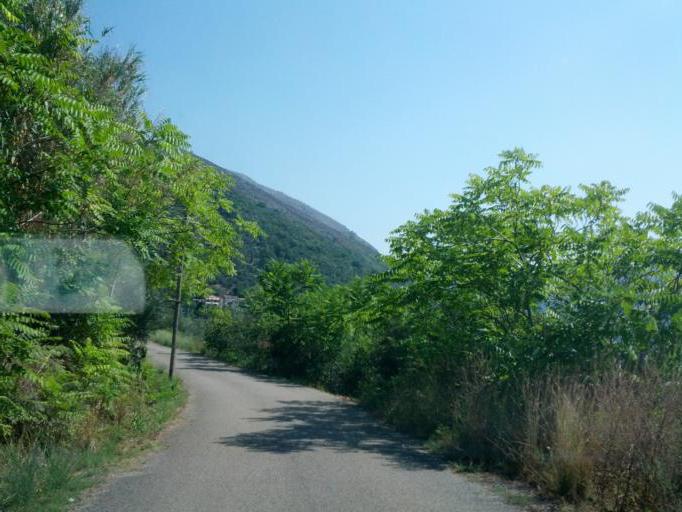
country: IT
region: Latium
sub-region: Provincia di Latina
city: Monte San Biagio
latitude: 41.3802
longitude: 13.3857
